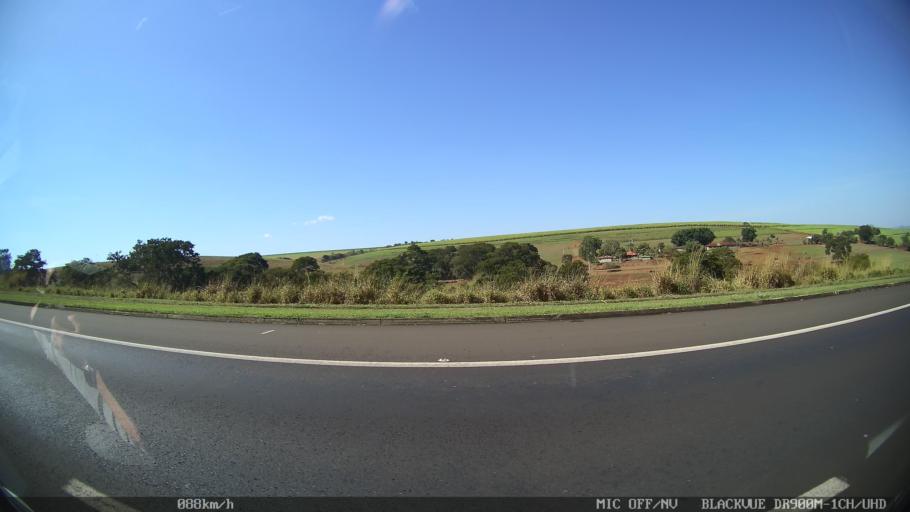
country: BR
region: Sao Paulo
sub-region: Franca
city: Franca
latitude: -20.6995
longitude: -47.5007
